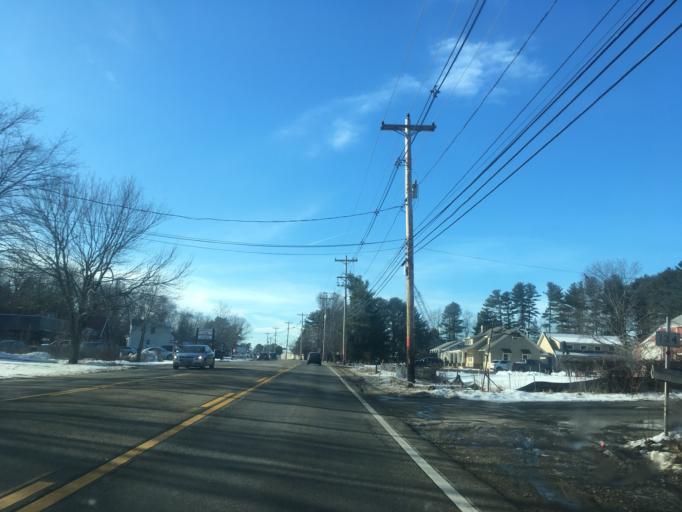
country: US
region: Massachusetts
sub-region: Essex County
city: Salisbury
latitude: 42.8444
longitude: -70.8840
